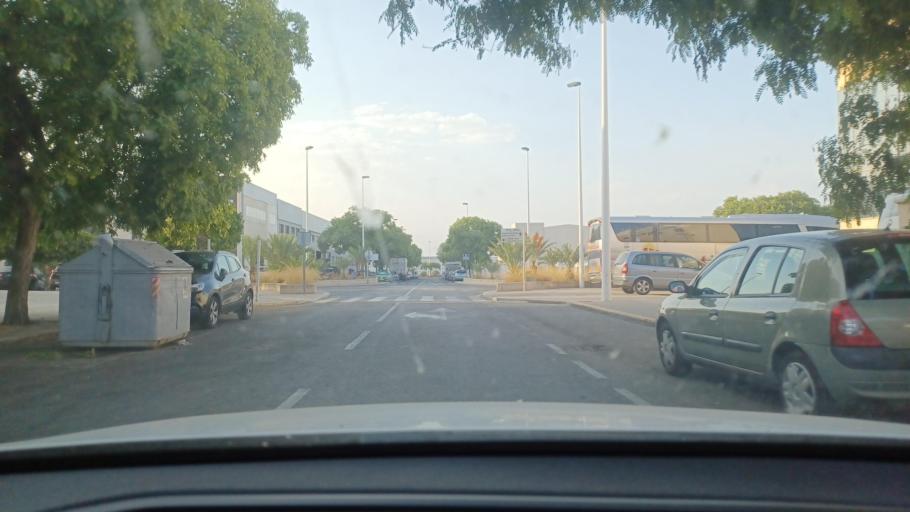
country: ES
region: Valencia
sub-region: Provincia de Alicante
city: Elche
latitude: 38.2943
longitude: -0.6197
